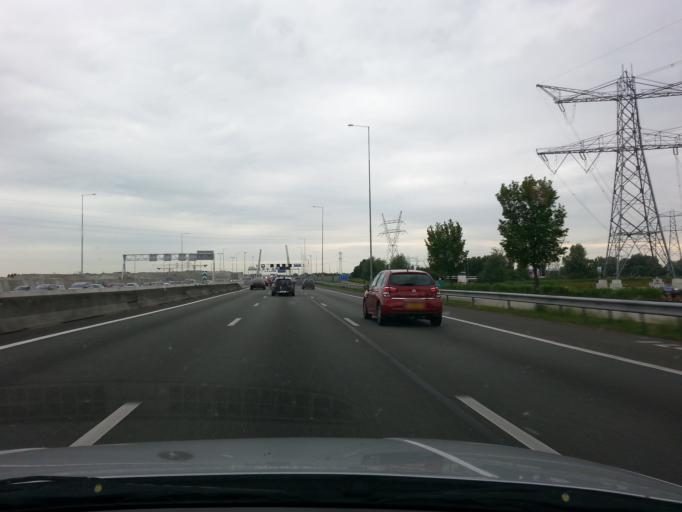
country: NL
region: North Holland
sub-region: Gemeente Weesp
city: Weesp
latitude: 52.3323
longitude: 5.0306
